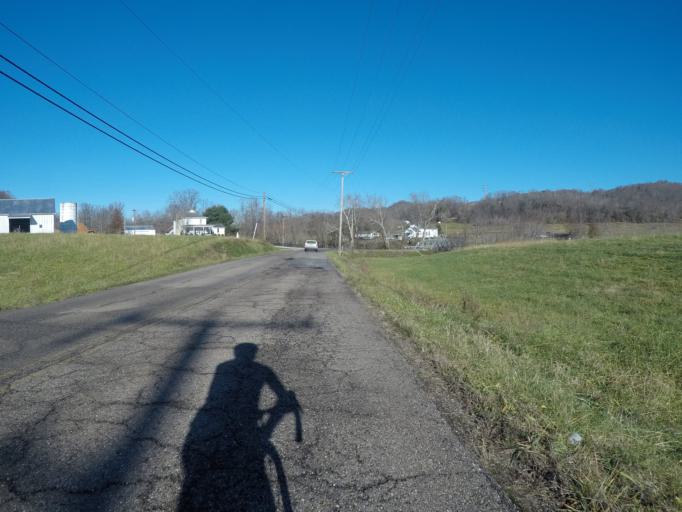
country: US
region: West Virginia
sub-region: Cabell County
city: Huntington
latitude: 38.4846
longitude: -82.4687
